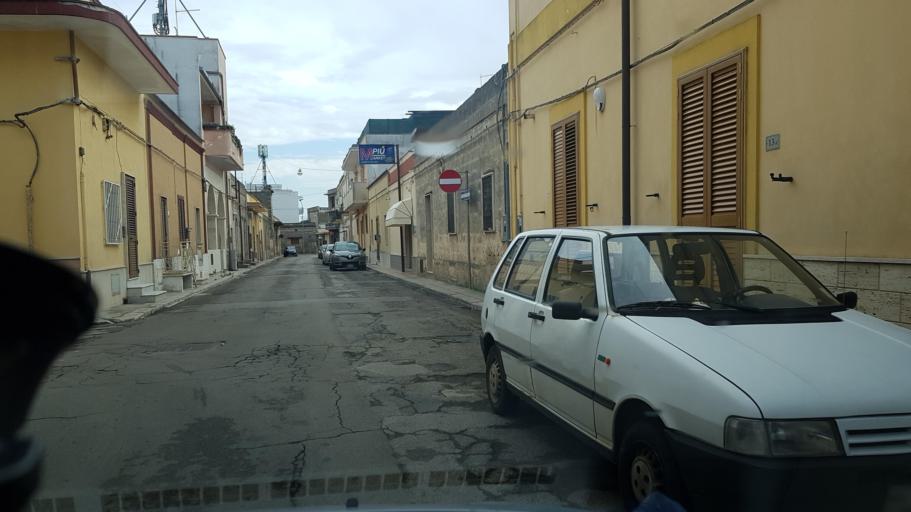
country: IT
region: Apulia
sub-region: Provincia di Brindisi
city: Torre Santa Susanna
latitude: 40.4704
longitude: 17.7408
